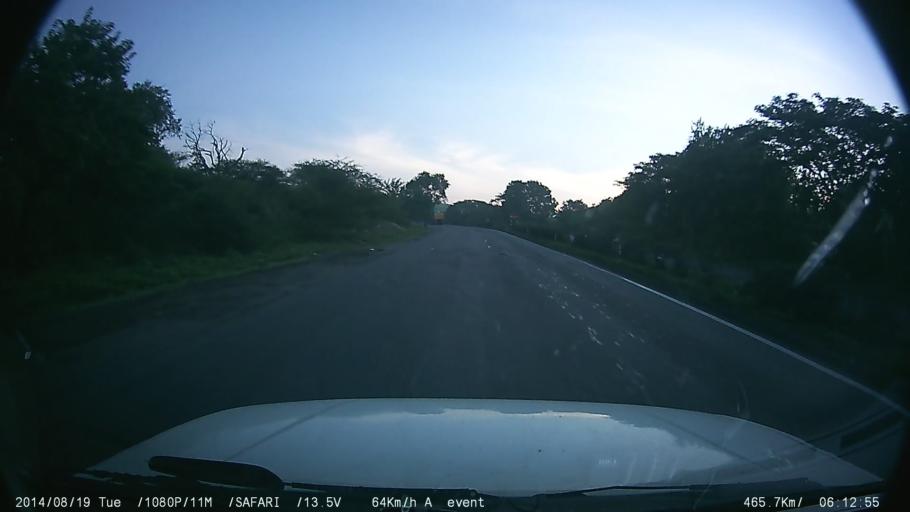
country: IN
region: Tamil Nadu
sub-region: Dharmapuri
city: Dharmapuri
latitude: 11.9616
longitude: 78.0503
